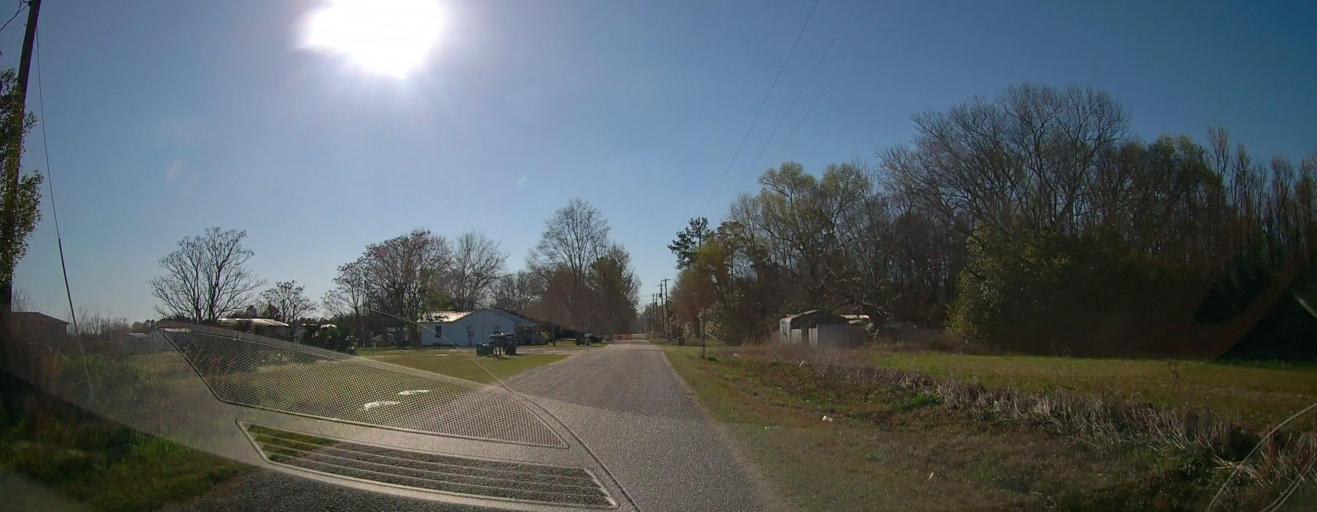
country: US
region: Georgia
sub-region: Taylor County
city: Reynolds
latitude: 32.5549
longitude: -84.0858
